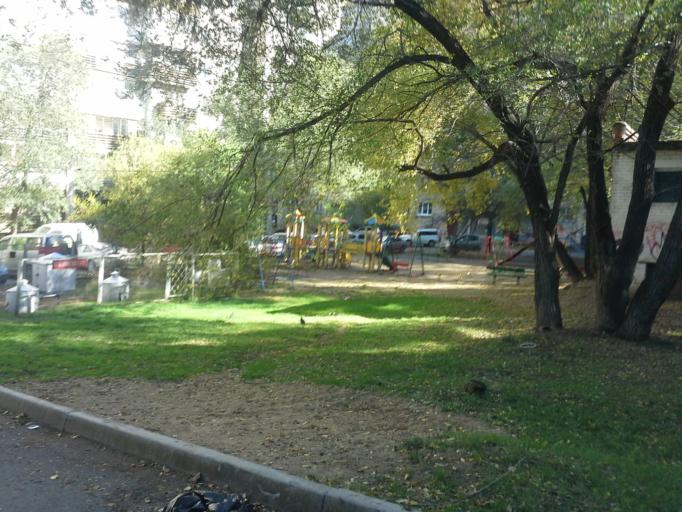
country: RU
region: Khabarovsk Krai
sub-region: Khabarovskiy Rayon
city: Khabarovsk
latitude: 48.4677
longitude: 135.0694
